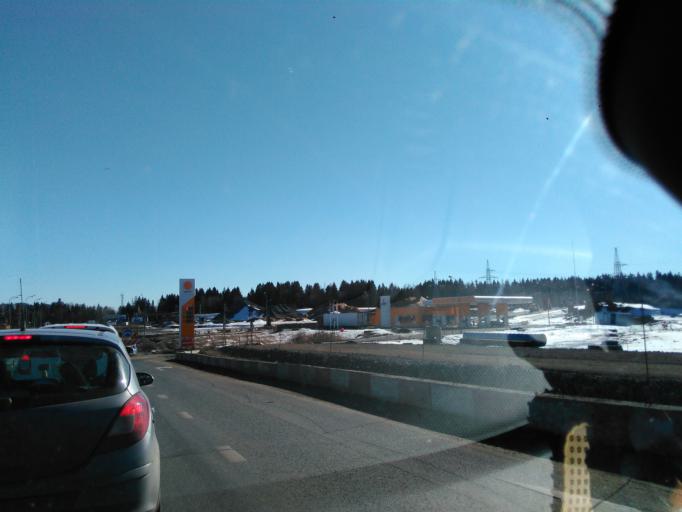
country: RU
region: Moskovskaya
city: Yermolino
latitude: 56.1416
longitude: 37.4935
